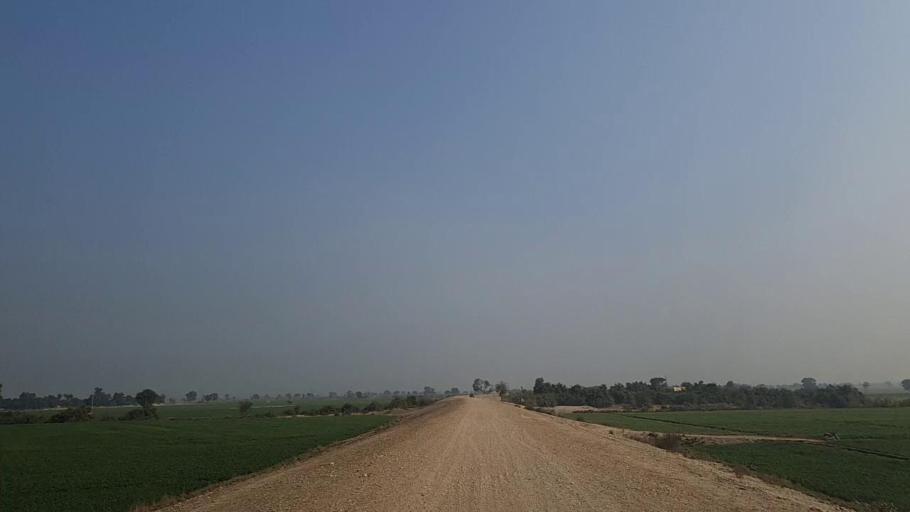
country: PK
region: Sindh
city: Sann
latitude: 26.0896
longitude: 68.1534
